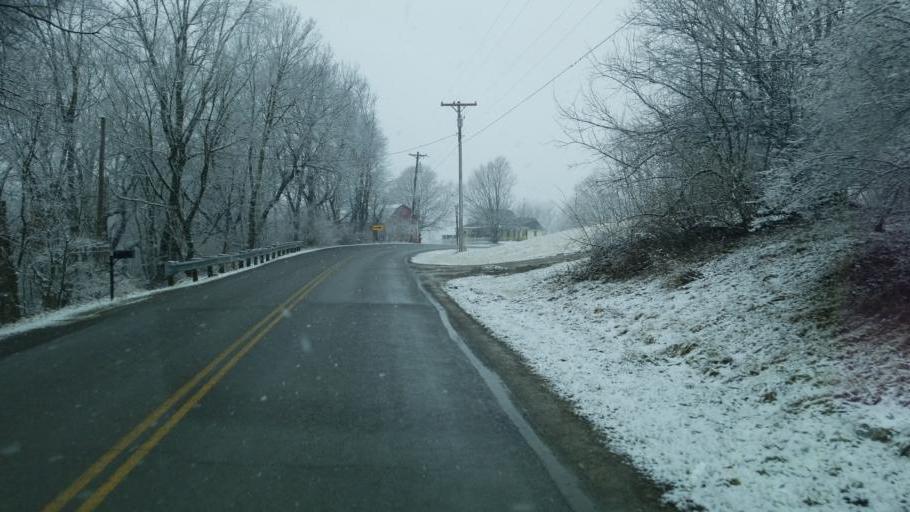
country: US
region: Ohio
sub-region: Logan County
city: Bellefontaine
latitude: 40.3284
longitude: -83.6666
